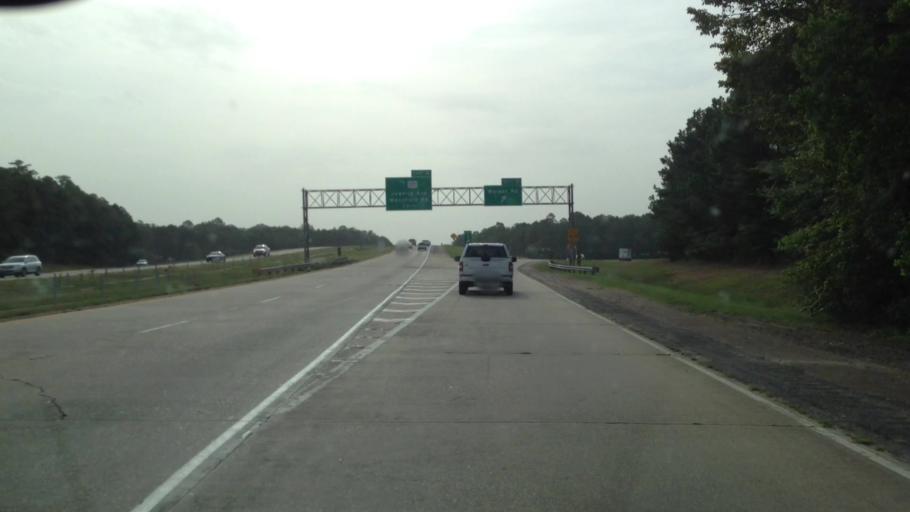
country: US
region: Louisiana
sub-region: Caddo Parish
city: Shreveport
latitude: 32.4172
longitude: -93.8194
